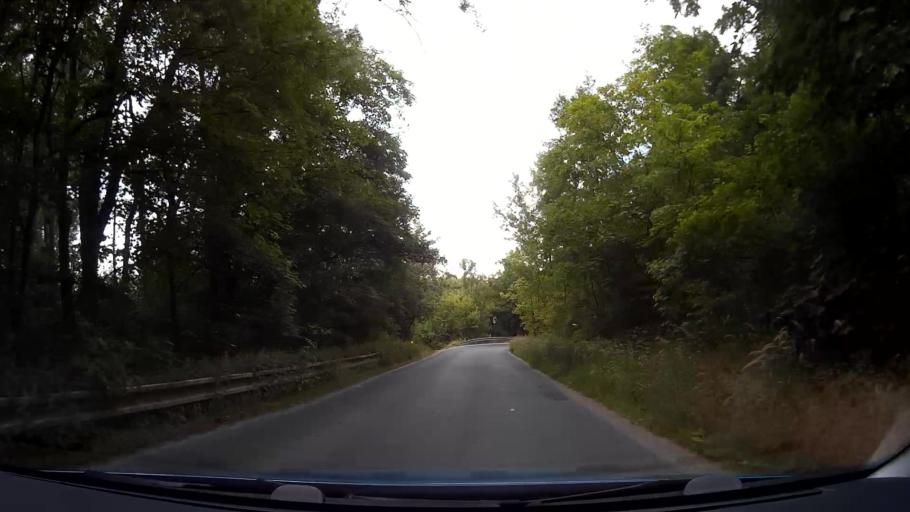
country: CZ
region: South Moravian
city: Orechov
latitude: 49.1227
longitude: 16.5261
